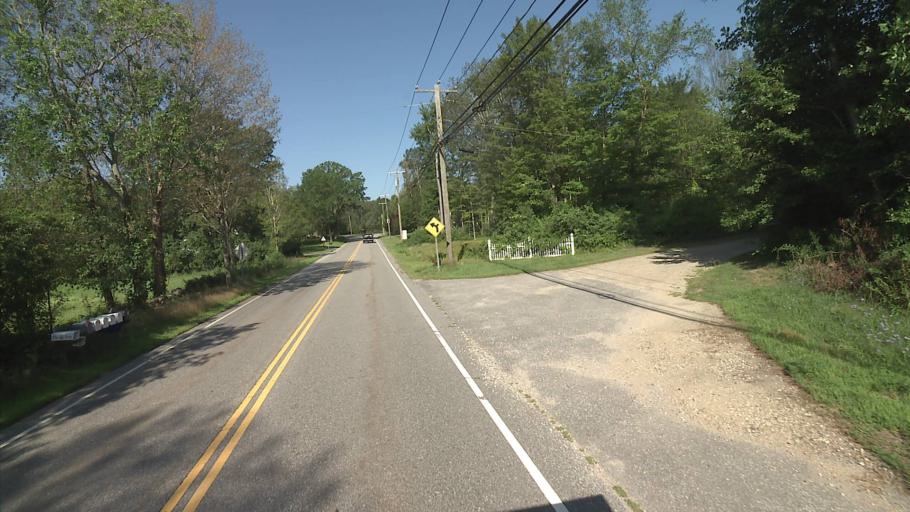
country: US
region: Connecticut
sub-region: New London County
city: Montville Center
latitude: 41.5417
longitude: -72.1858
